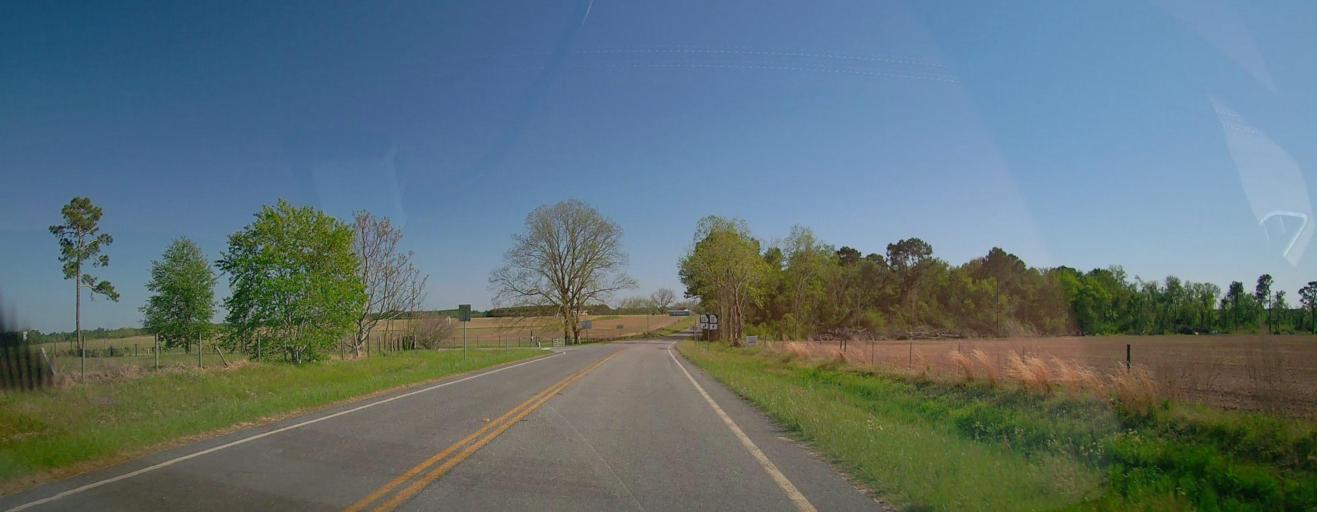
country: US
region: Georgia
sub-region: Wilcox County
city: Rochelle
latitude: 31.9772
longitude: -83.4565
